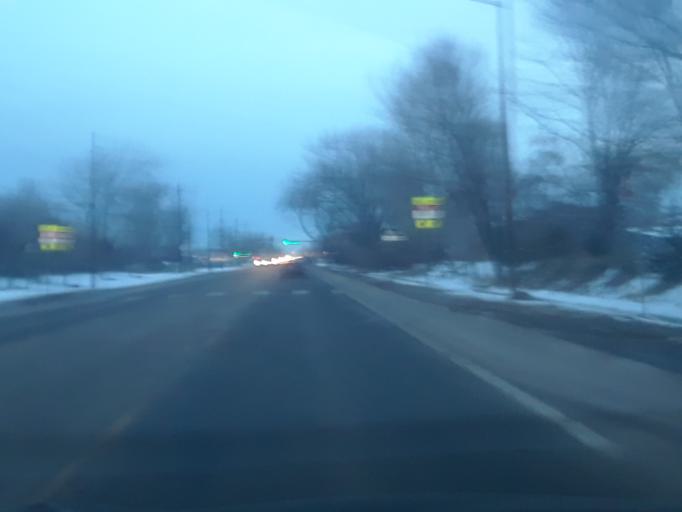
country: US
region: Colorado
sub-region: Boulder County
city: Boulder
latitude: 40.0527
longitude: -105.2821
